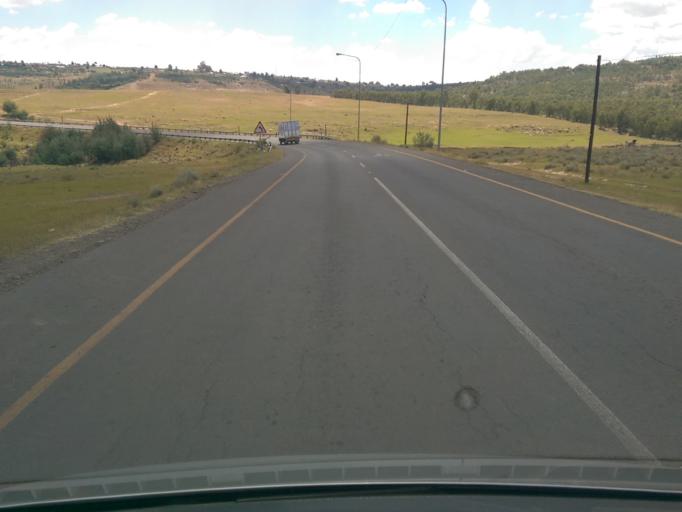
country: LS
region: Maseru
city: Maseru
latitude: -29.3910
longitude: 27.5516
